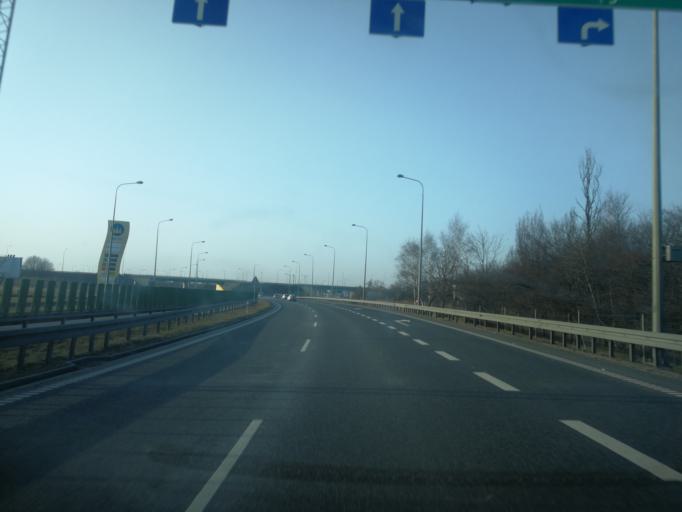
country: PL
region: Warmian-Masurian Voivodeship
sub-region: Powiat elblaski
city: Gronowo Gorne
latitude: 54.1356
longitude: 19.4540
